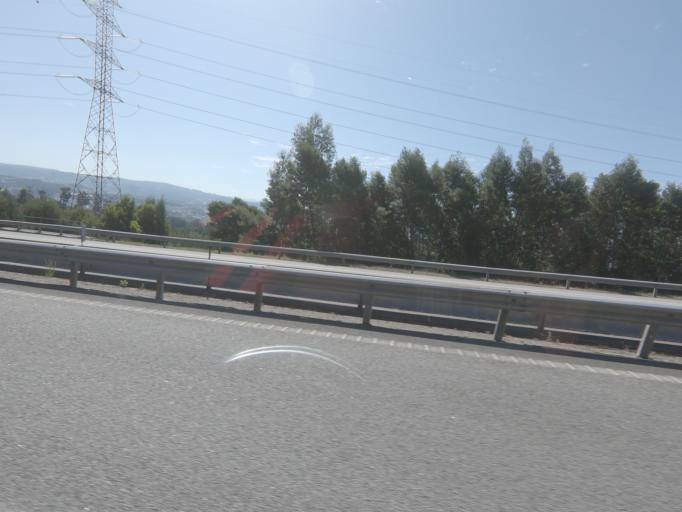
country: PT
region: Porto
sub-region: Paredes
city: Baltar
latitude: 41.1870
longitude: -8.3660
